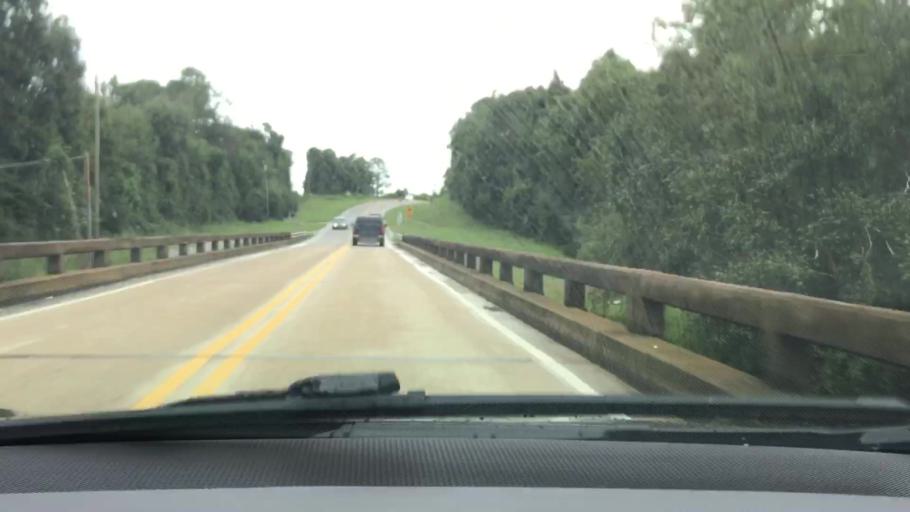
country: US
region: Alabama
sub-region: Geneva County
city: Samson
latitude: 31.0435
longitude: -86.1014
